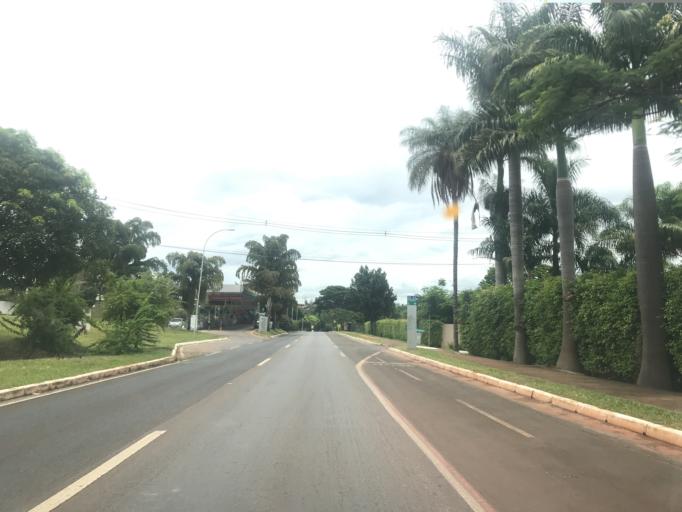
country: BR
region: Federal District
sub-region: Brasilia
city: Brasilia
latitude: -15.8372
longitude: -47.8366
